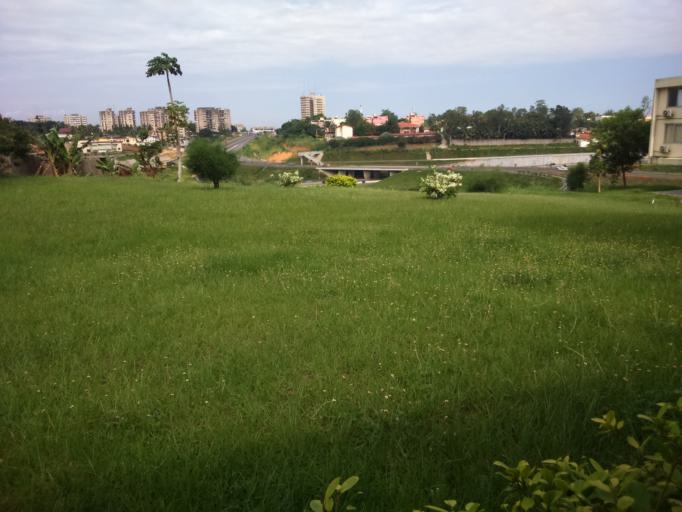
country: CI
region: Lagunes
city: Abidjan
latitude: 5.3411
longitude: -3.9851
